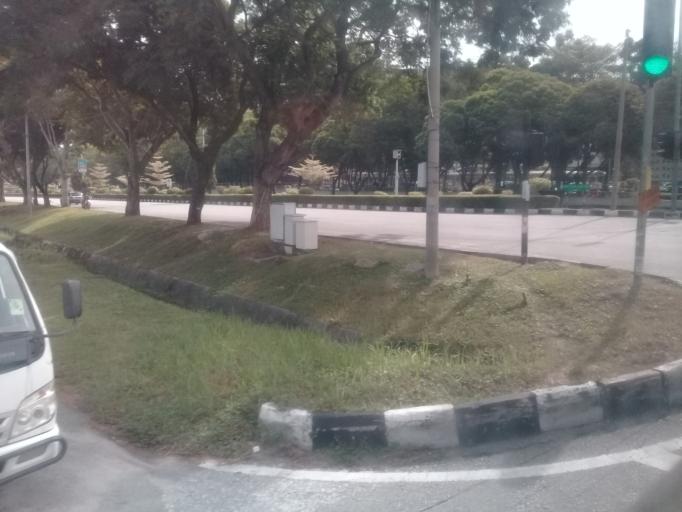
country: MY
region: Perak
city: Ipoh
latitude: 4.6124
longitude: 101.1172
